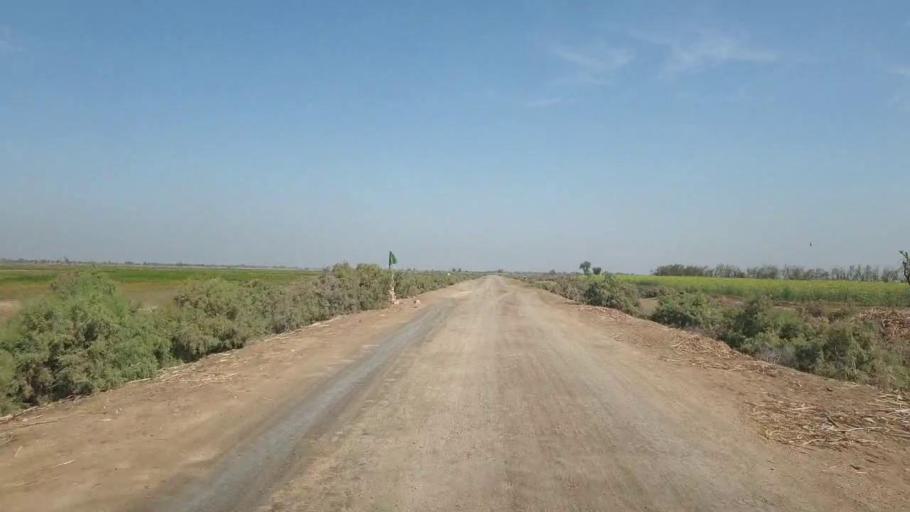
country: PK
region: Sindh
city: Samaro
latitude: 25.3500
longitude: 69.2515
